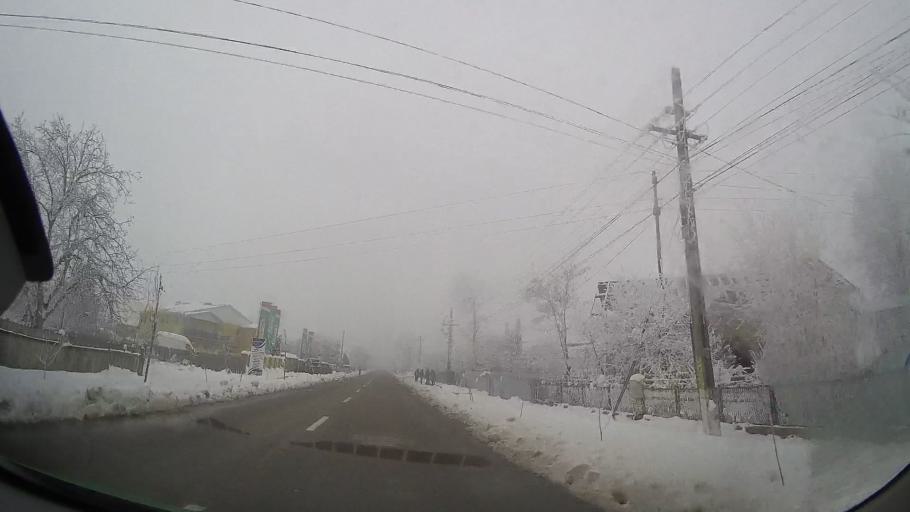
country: RO
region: Iasi
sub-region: Municipiul Pascani
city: Pascani
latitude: 47.2583
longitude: 26.7125
